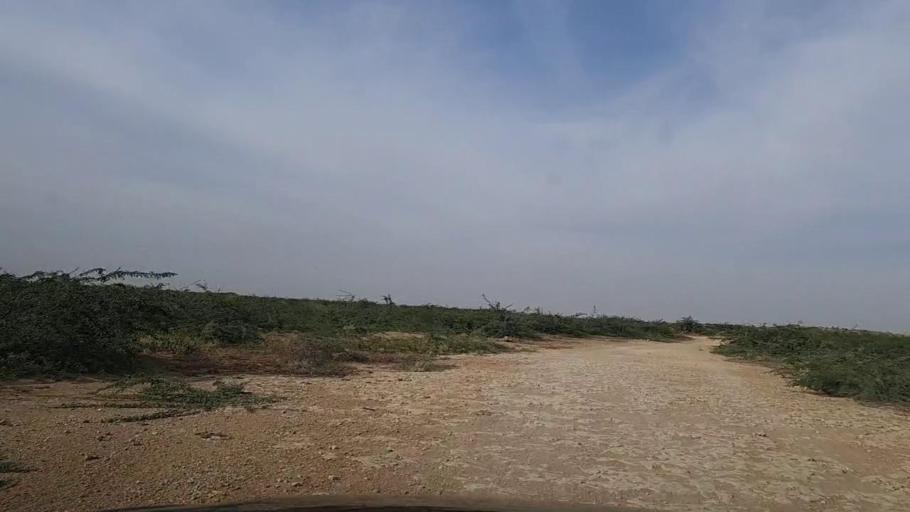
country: PK
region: Sindh
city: Gharo
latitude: 24.7830
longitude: 67.5600
